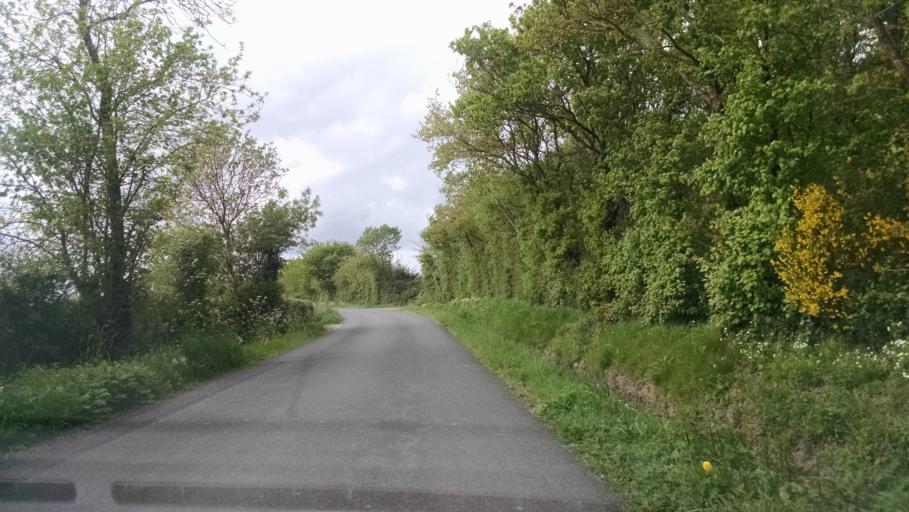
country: FR
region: Pays de la Loire
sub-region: Departement de la Vendee
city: Saint-Hilaire-de-Loulay
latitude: 46.9835
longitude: -1.3343
